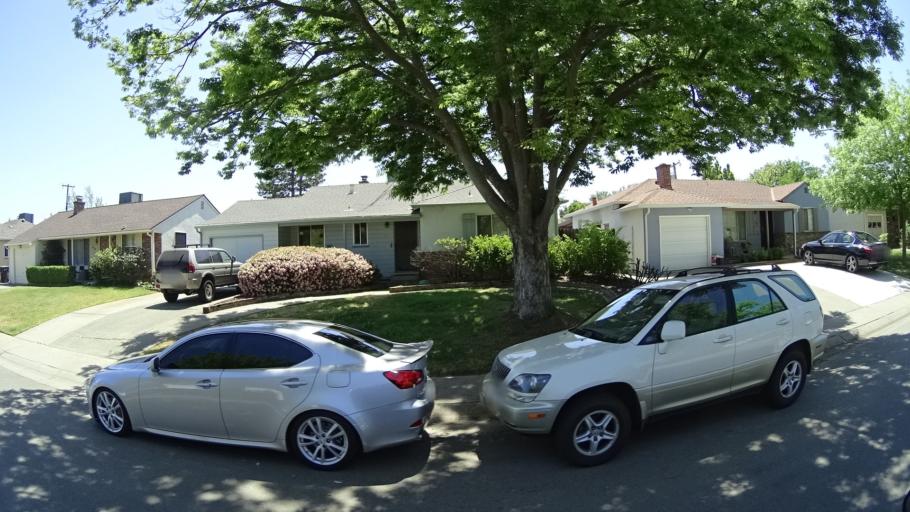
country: US
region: California
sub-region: Sacramento County
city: Parkway
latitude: 38.5223
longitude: -121.4817
